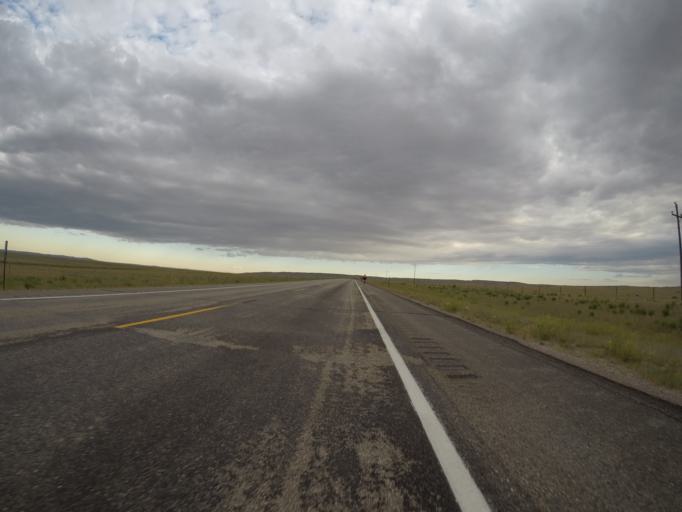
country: US
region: Wyoming
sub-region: Albany County
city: Laramie
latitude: 41.8499
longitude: -106.0406
